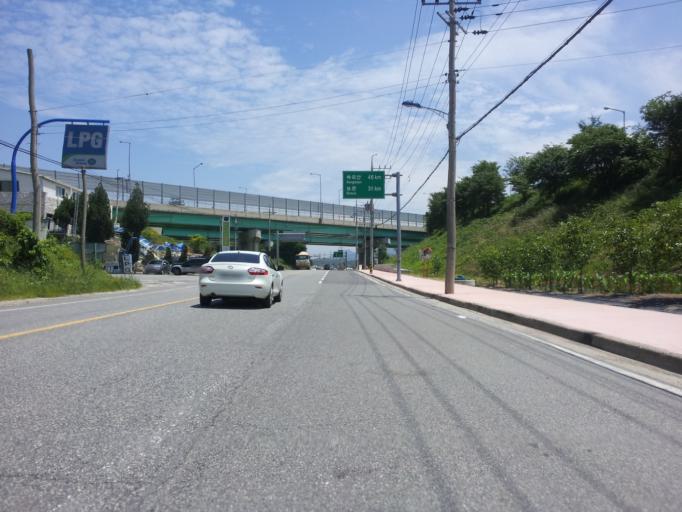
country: KR
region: Chungcheongbuk-do
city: Okcheon
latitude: 36.3113
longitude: 127.5661
